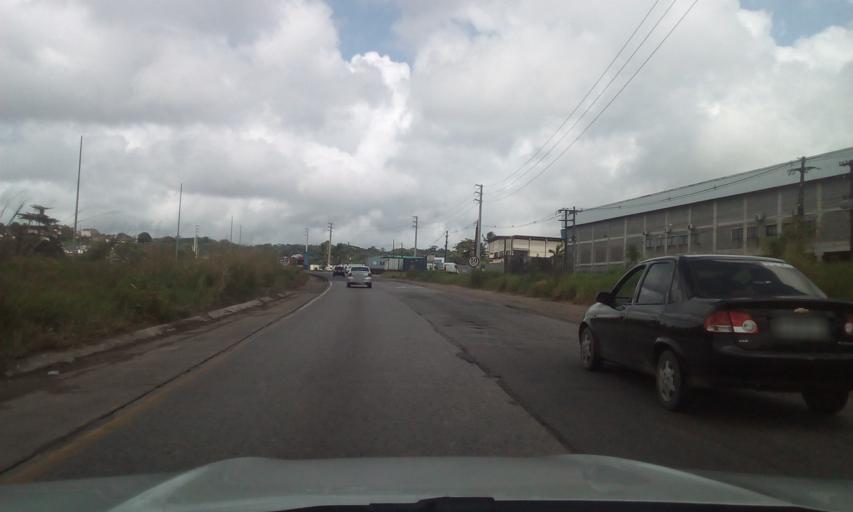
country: BR
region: Pernambuco
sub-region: Paulista
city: Paulista
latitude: -7.9891
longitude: -34.9352
